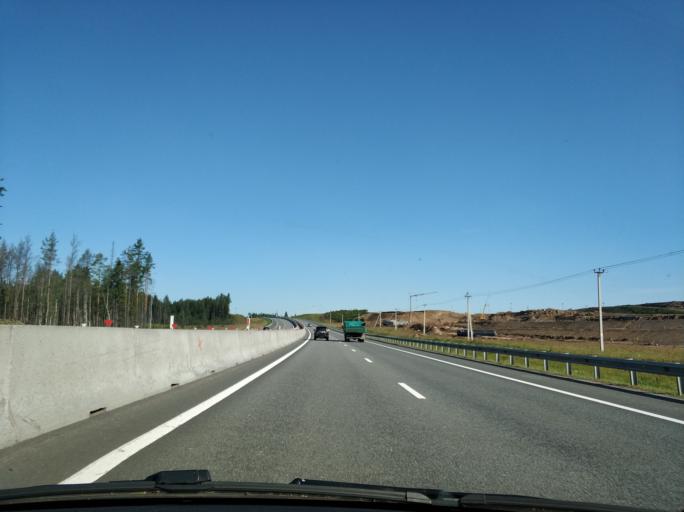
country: RU
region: Leningrad
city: Sosnovo
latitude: 60.5087
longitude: 30.1908
